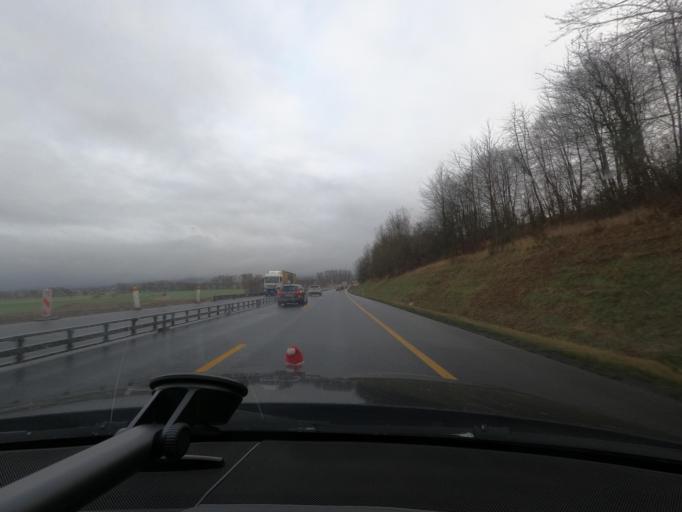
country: DE
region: Lower Saxony
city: Hillerse
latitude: 51.7203
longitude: 9.9458
